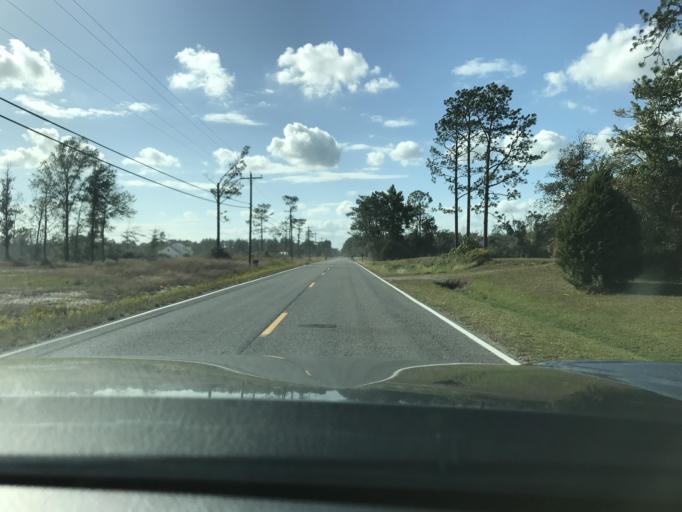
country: US
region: Louisiana
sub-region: Calcasieu Parish
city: Moss Bluff
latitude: 30.3226
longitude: -93.2624
